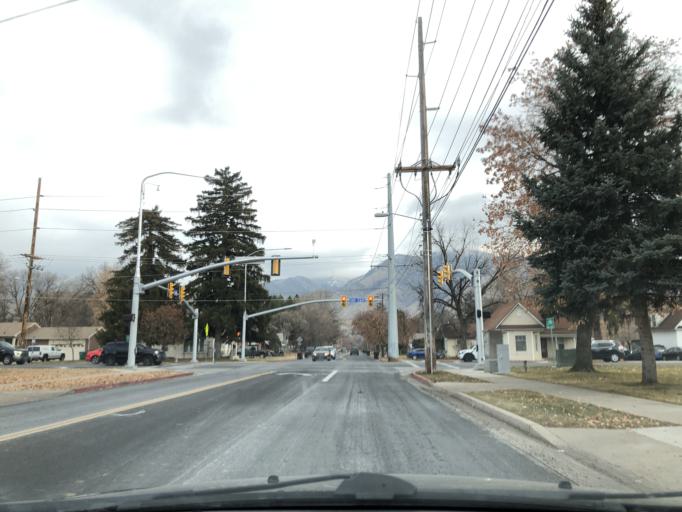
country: US
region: Utah
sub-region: Cache County
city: Logan
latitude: 41.7259
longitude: -111.8331
